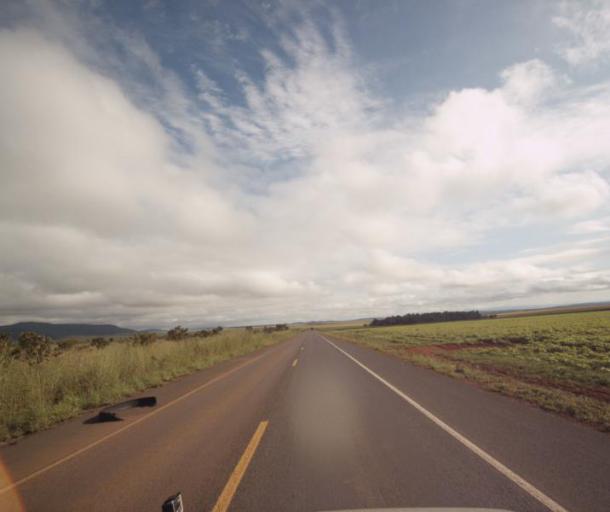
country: BR
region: Goias
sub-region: Padre Bernardo
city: Padre Bernardo
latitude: -15.4241
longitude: -48.6227
